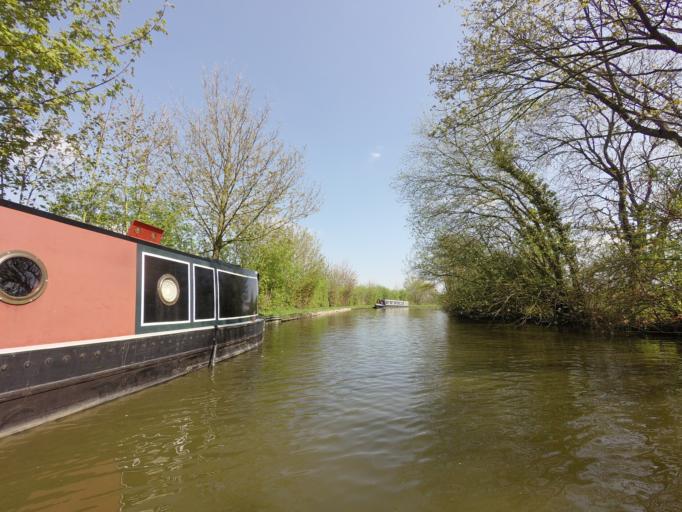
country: GB
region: England
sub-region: Buckinghamshire
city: Cheddington
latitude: 51.8444
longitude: -0.6483
